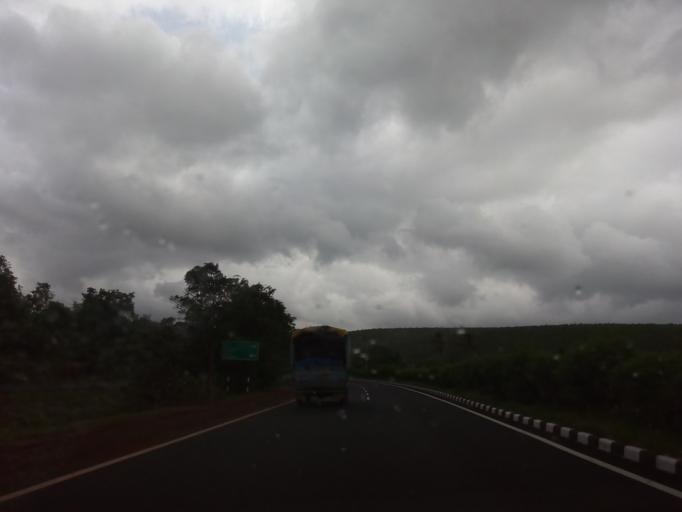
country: IN
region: Karnataka
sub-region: Belgaum
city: Hukeri
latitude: 16.0539
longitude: 74.5133
